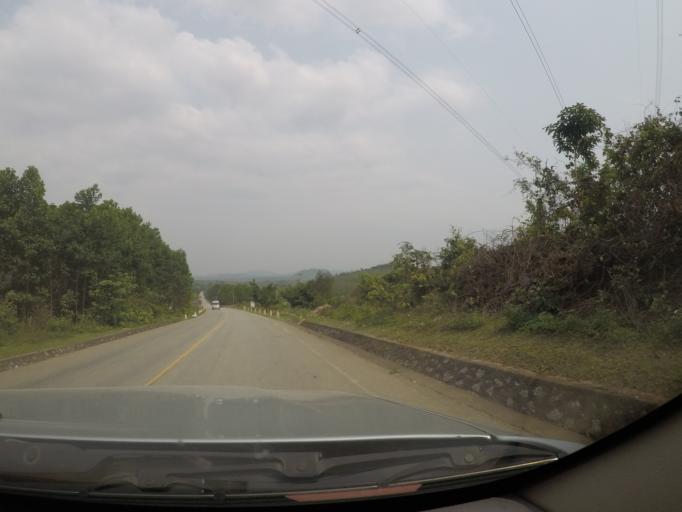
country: VN
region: Thanh Hoa
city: Thi Tran Yen Cat
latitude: 19.4749
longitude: 105.4187
